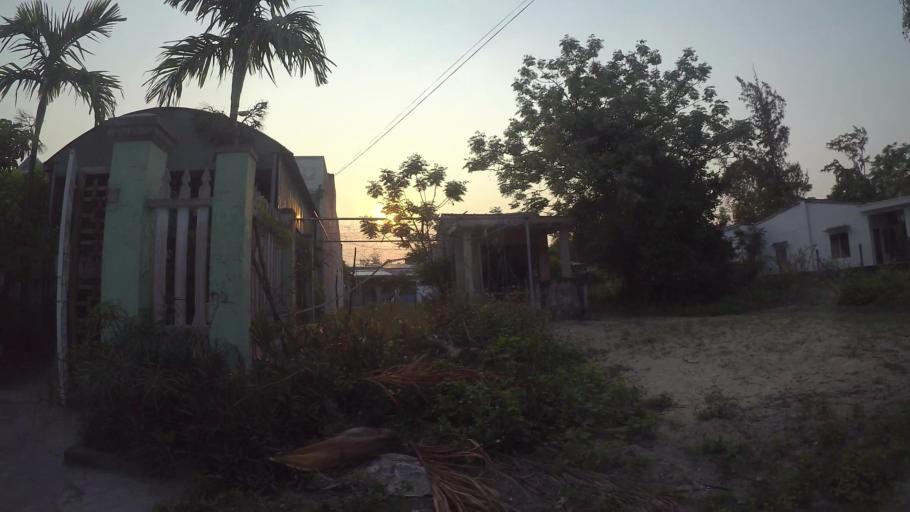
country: VN
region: Da Nang
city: Ngu Hanh Son
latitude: 15.9550
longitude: 108.2535
